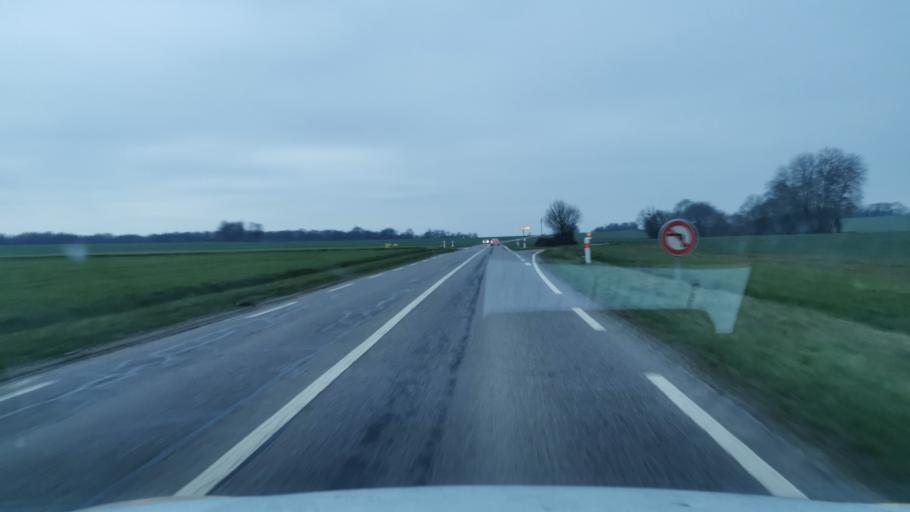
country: FR
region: Ile-de-France
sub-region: Departement des Yvelines
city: Longnes
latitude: 48.9370
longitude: 1.6320
